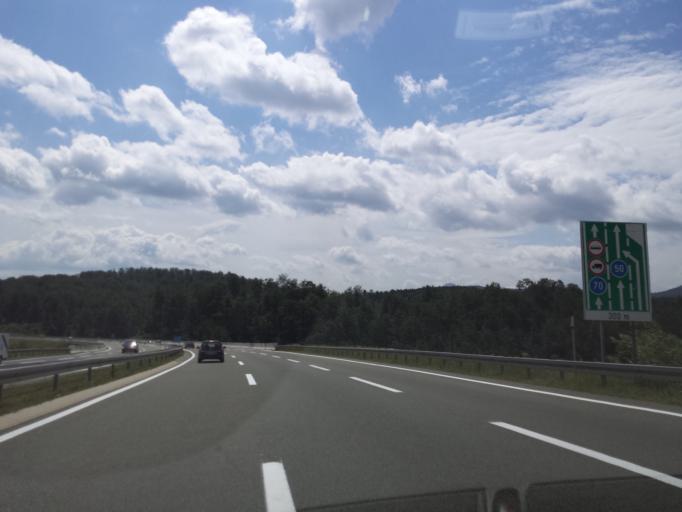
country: HR
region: Primorsko-Goranska
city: Vrbovsko
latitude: 45.3599
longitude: 15.0631
